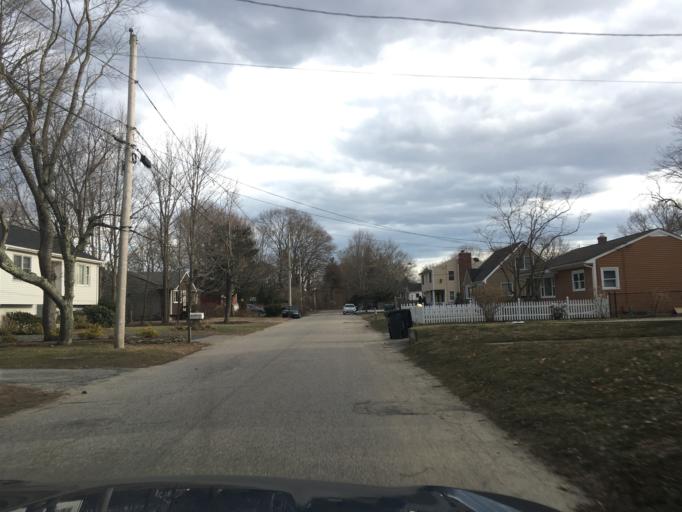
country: US
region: Rhode Island
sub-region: Kent County
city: East Greenwich
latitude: 41.6621
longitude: -71.4211
